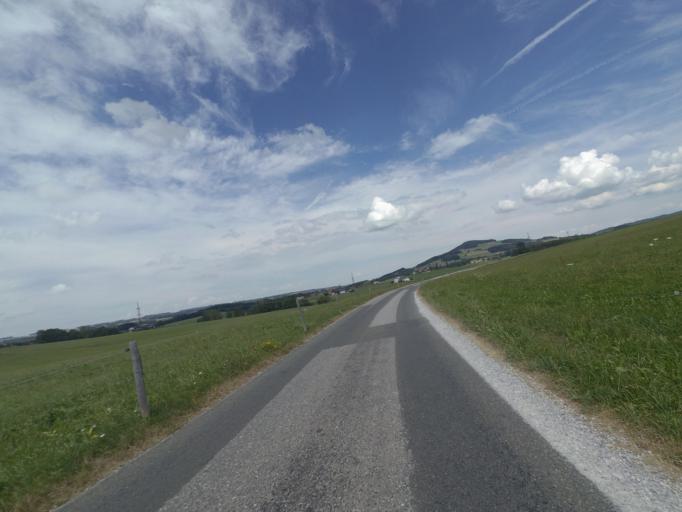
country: AT
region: Salzburg
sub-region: Politischer Bezirk Salzburg-Umgebung
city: Obertrum am See
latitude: 47.9206
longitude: 13.1041
